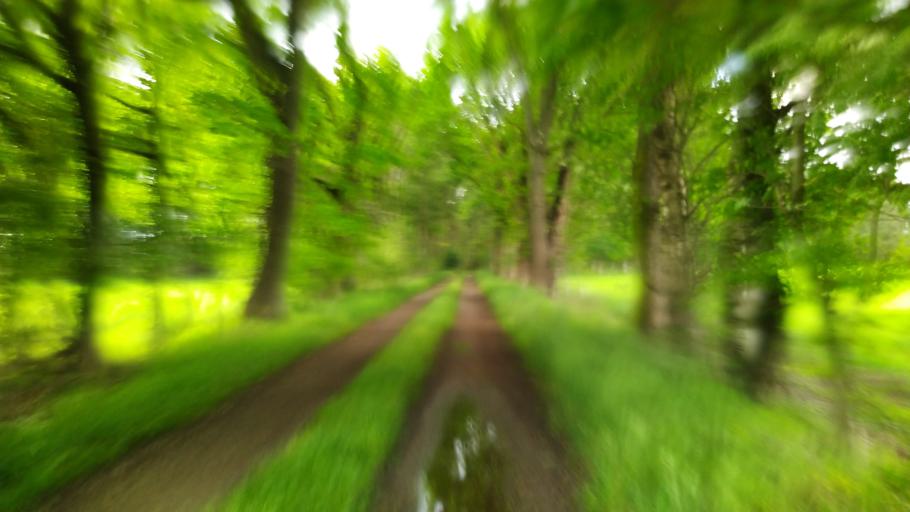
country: DE
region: Lower Saxony
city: Brest
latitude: 53.4211
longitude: 9.3584
